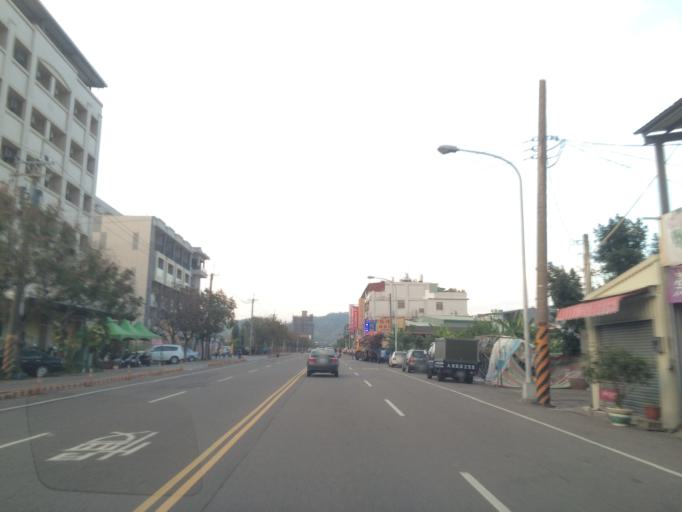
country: TW
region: Taiwan
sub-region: Taichung City
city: Taichung
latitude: 24.1628
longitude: 120.7334
